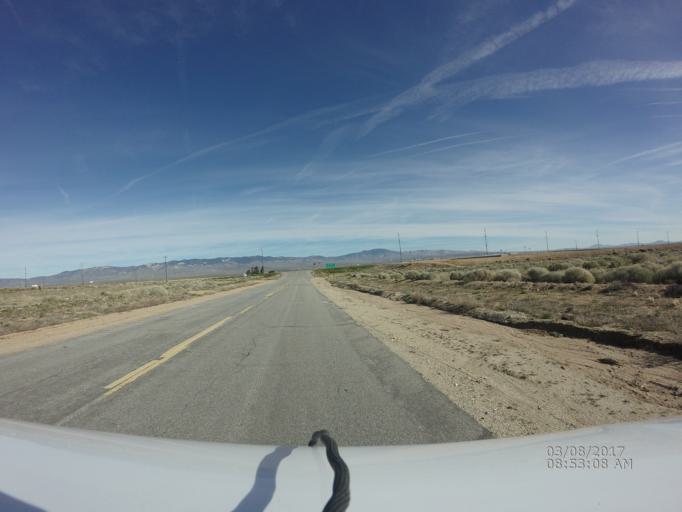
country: US
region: California
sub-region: Los Angeles County
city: Green Valley
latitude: 34.7731
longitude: -118.5626
